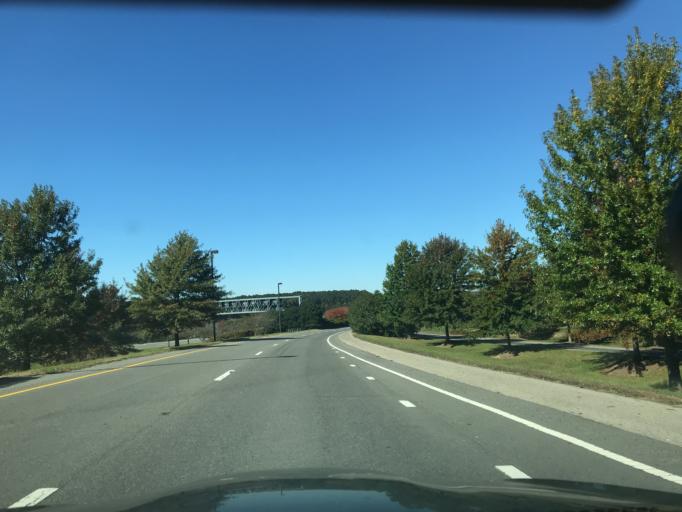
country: US
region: North Carolina
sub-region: Wake County
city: Morrisville
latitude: 35.8689
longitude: -78.8049
